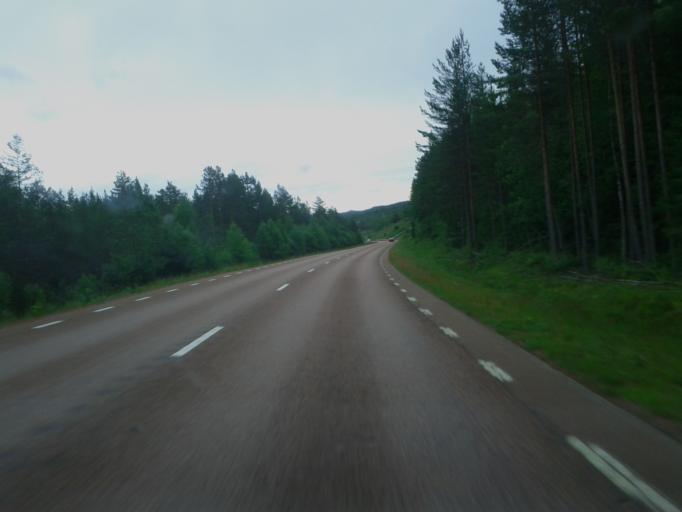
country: SE
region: Dalarna
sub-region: Alvdalens Kommun
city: AElvdalen
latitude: 61.2744
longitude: 13.7861
